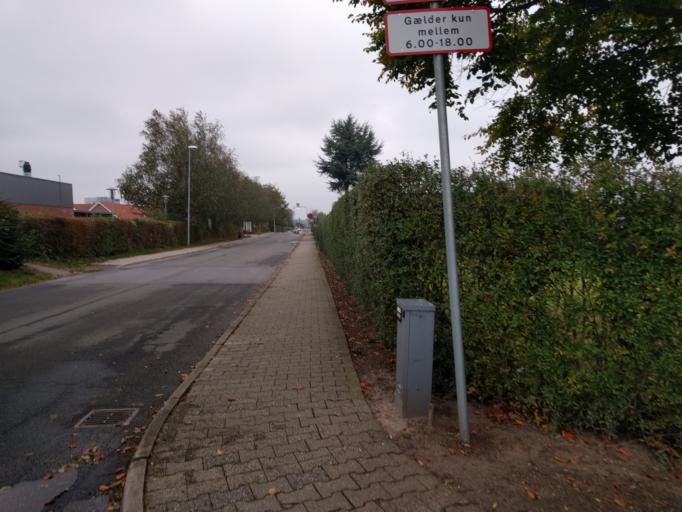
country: DK
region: South Denmark
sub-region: Fredericia Kommune
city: Snoghoj
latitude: 55.5406
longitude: 9.7101
